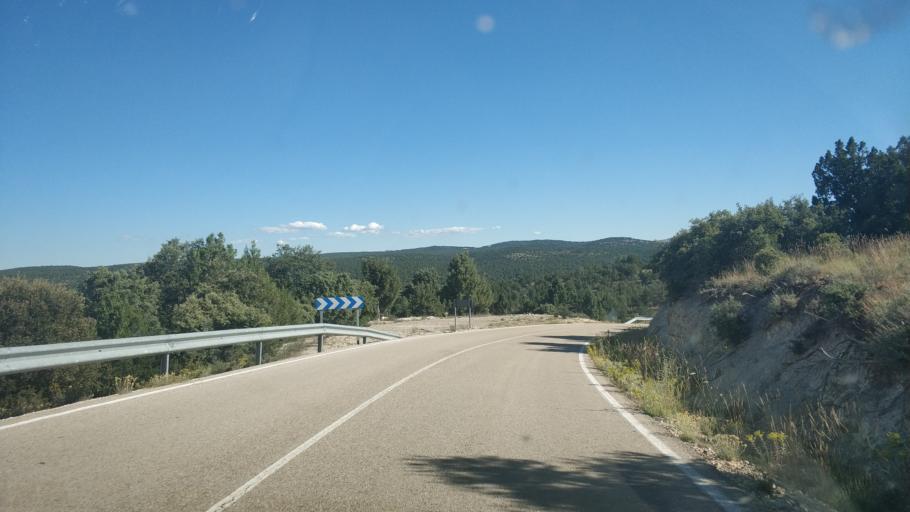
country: ES
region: Castille and Leon
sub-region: Provincia de Soria
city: Liceras
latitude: 41.4450
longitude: -3.2164
